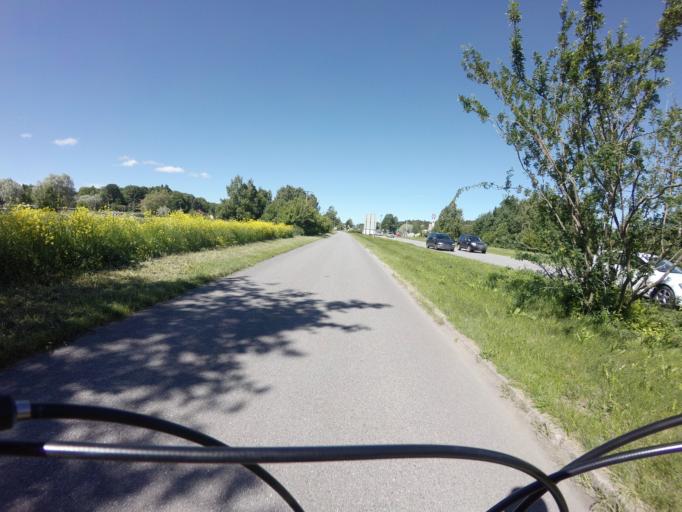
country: FI
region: Varsinais-Suomi
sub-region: Turku
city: Turku
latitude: 60.4568
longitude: 22.2318
